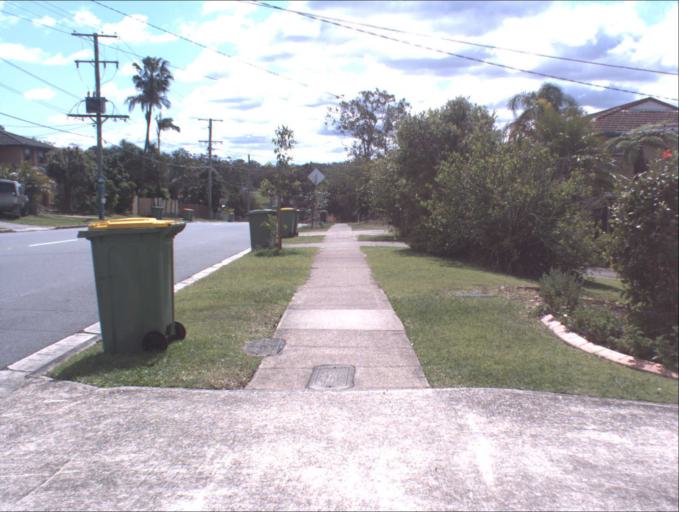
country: AU
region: Queensland
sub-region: Brisbane
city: Sunnybank Hills
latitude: -27.6635
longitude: 153.0293
